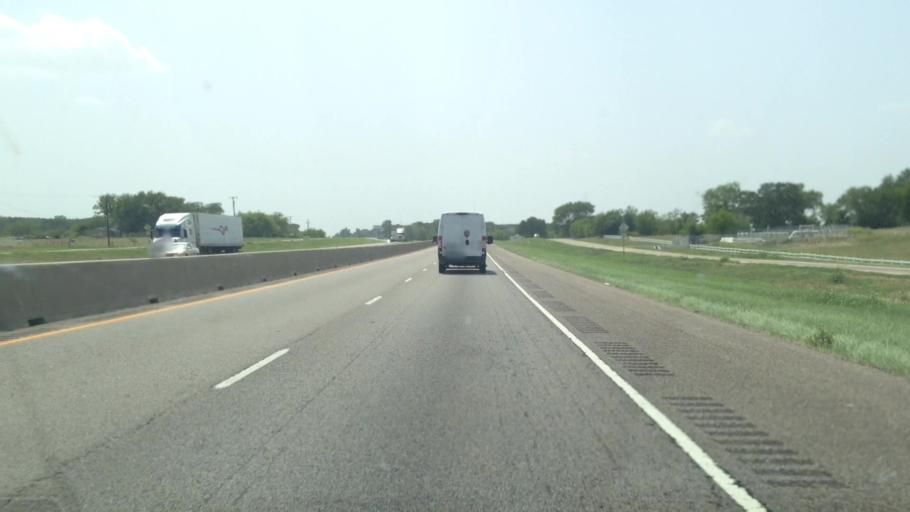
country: US
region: Texas
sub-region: Hopkins County
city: Sulphur Springs
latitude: 33.1479
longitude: -95.5282
